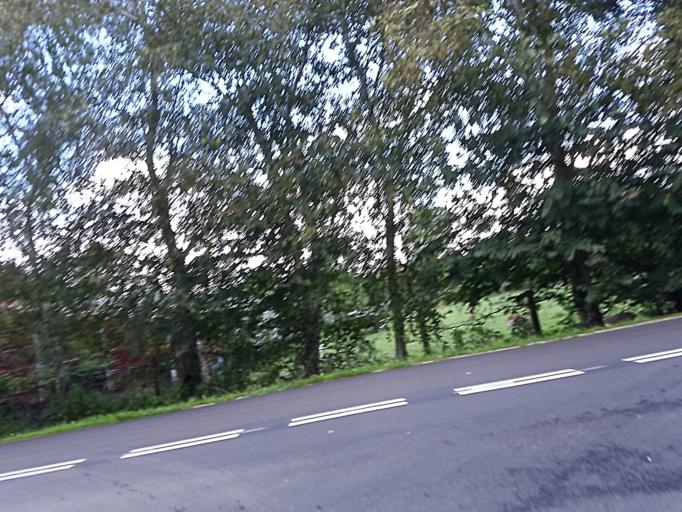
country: DK
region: Capital Region
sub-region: Egedal Kommune
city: Stenlose
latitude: 55.7395
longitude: 12.1917
